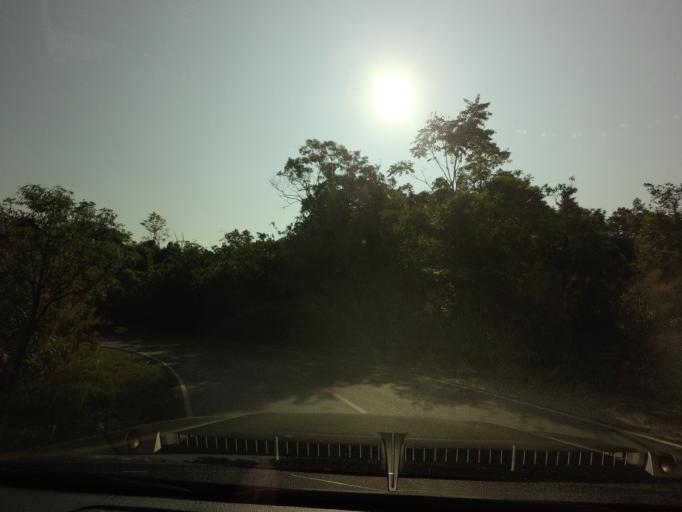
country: TH
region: Kanchanaburi
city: Thong Pha Phum
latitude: 14.6756
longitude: 98.3755
